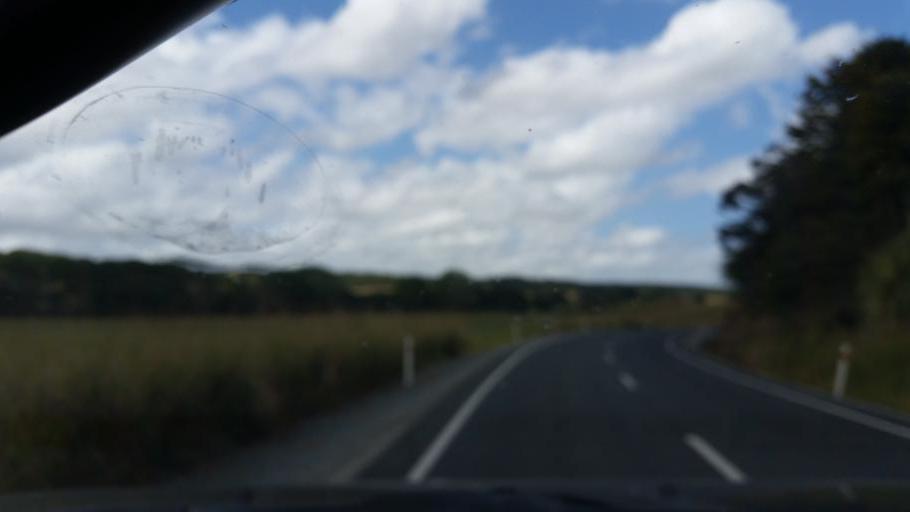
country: NZ
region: Northland
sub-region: Kaipara District
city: Dargaville
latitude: -35.8524
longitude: 173.8474
